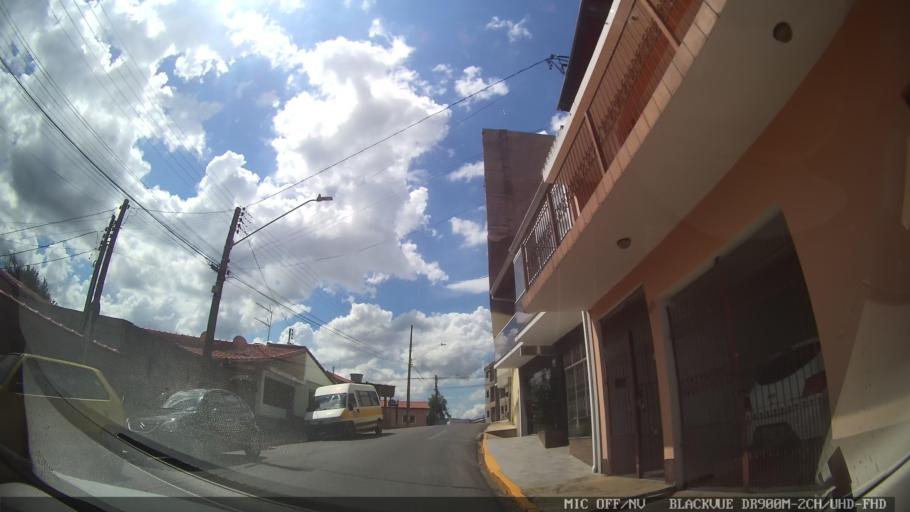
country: BR
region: Minas Gerais
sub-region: Extrema
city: Extrema
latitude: -22.8577
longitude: -46.3213
